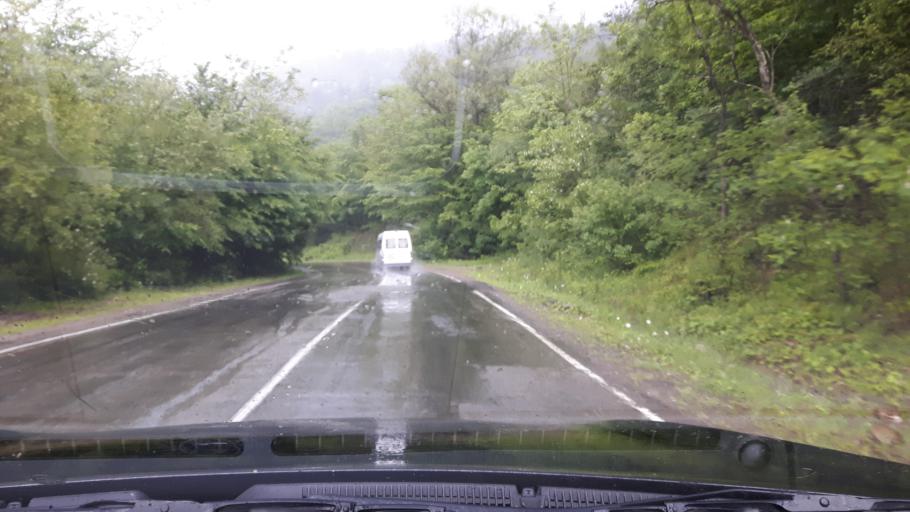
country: GE
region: Kakheti
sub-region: Telavi
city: Telavi
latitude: 41.8978
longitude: 45.3688
